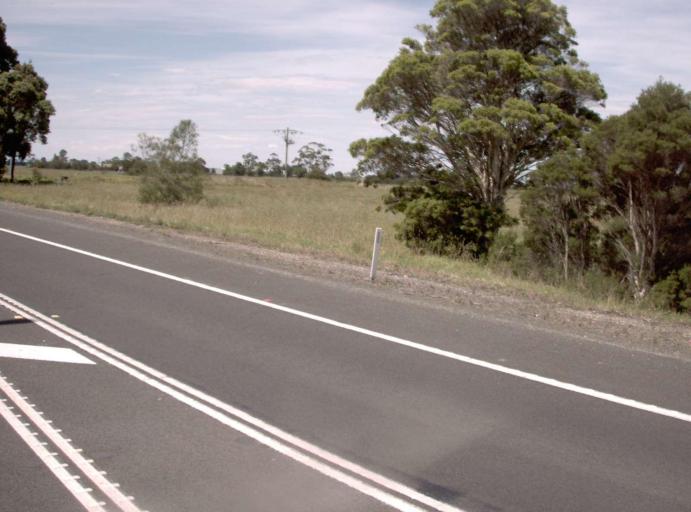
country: AU
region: Victoria
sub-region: Wellington
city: Sale
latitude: -38.0693
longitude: 147.0737
